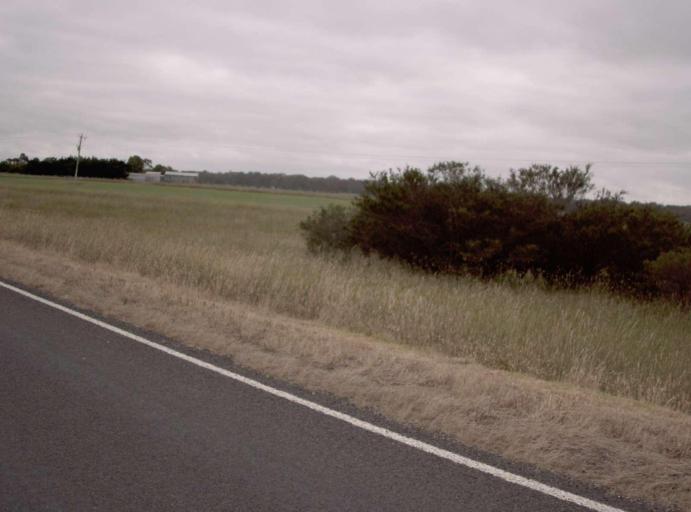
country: AU
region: Victoria
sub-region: Wellington
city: Sale
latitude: -38.0790
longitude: 146.9887
